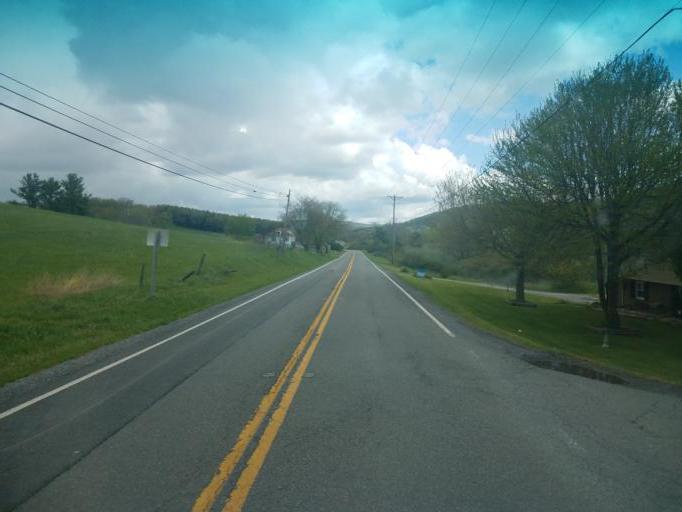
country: US
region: Virginia
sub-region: Bland County
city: Bland
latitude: 37.0863
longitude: -81.1441
